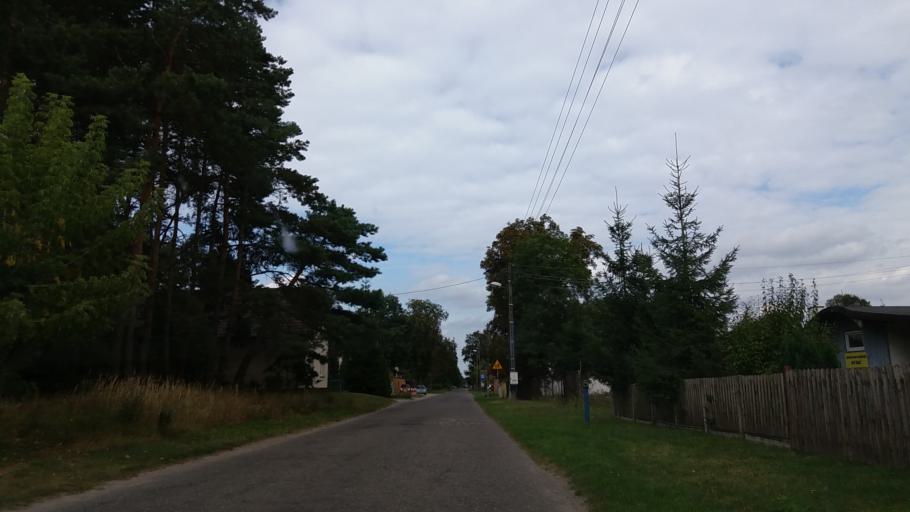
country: PL
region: West Pomeranian Voivodeship
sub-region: Powiat stargardzki
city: Kobylanka
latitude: 53.3357
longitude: 14.8917
